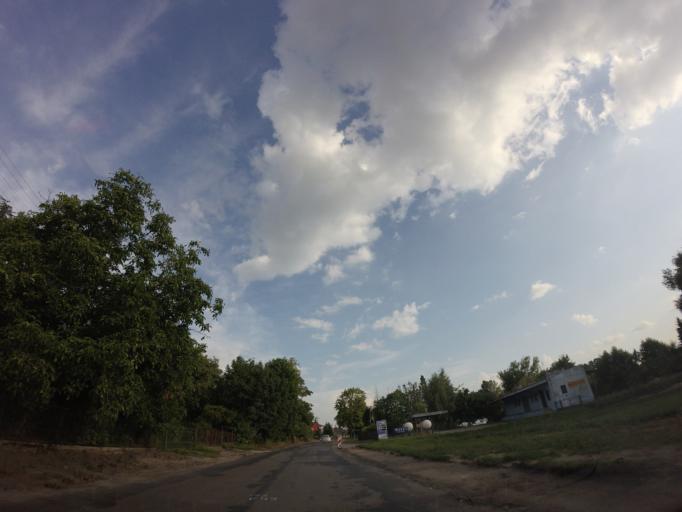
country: PL
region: Lublin Voivodeship
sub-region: Powiat lubartowski
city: Przytoczno
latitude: 51.6182
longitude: 22.2727
